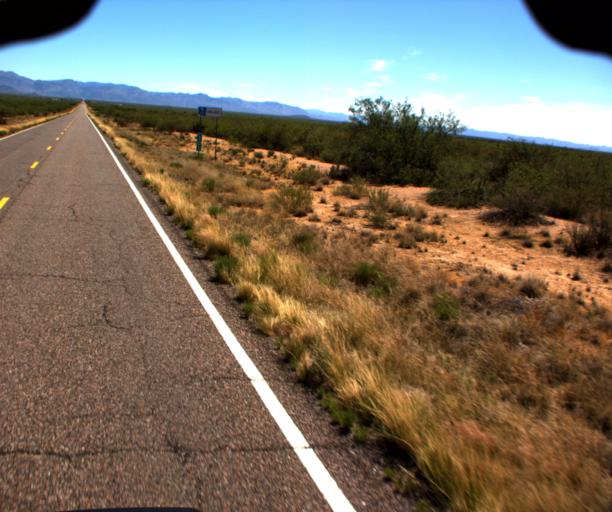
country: US
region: Arizona
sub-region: Yavapai County
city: Congress
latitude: 34.1112
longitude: -112.9814
